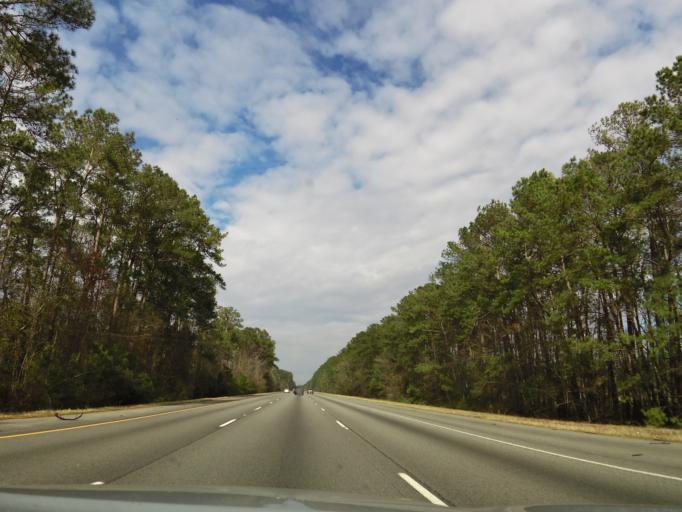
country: US
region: Georgia
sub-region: Bryan County
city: Richmond Hill
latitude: 31.8740
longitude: -81.3317
